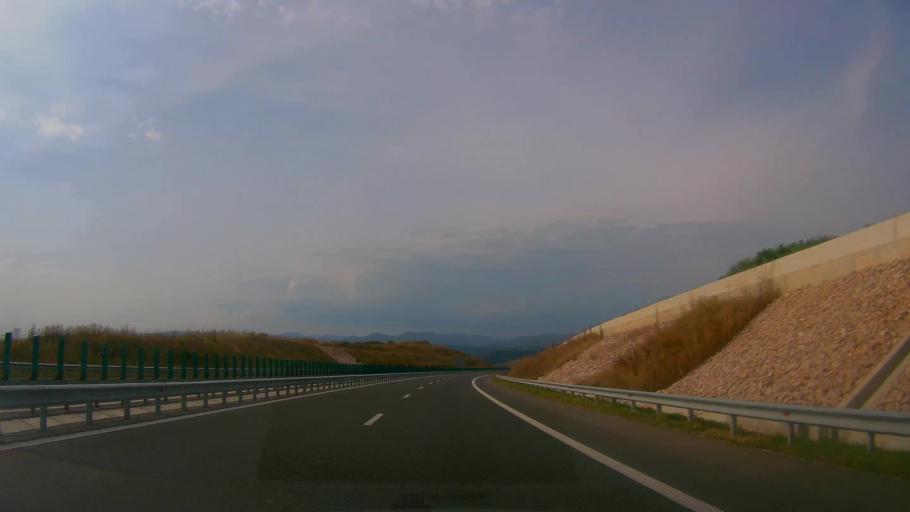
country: RO
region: Cluj
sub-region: Comuna Floresti
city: Luna de Sus
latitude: 46.7785
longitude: 23.4106
